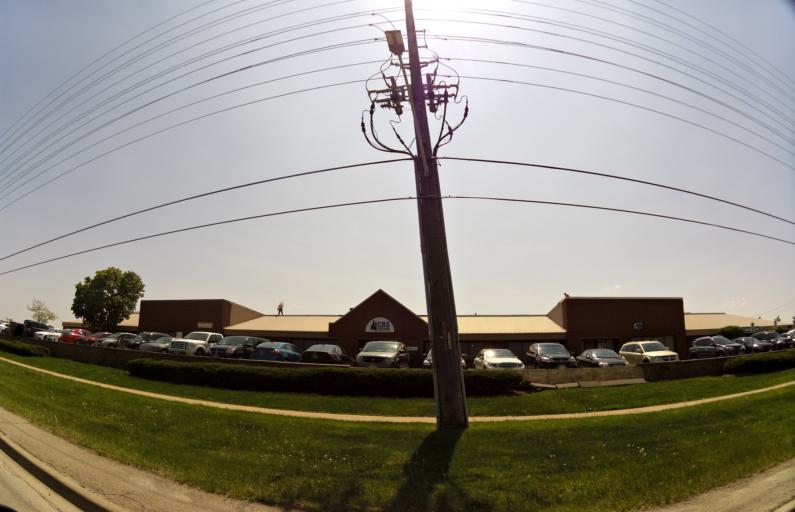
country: CA
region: Ontario
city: Mississauga
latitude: 43.6385
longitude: -79.6485
